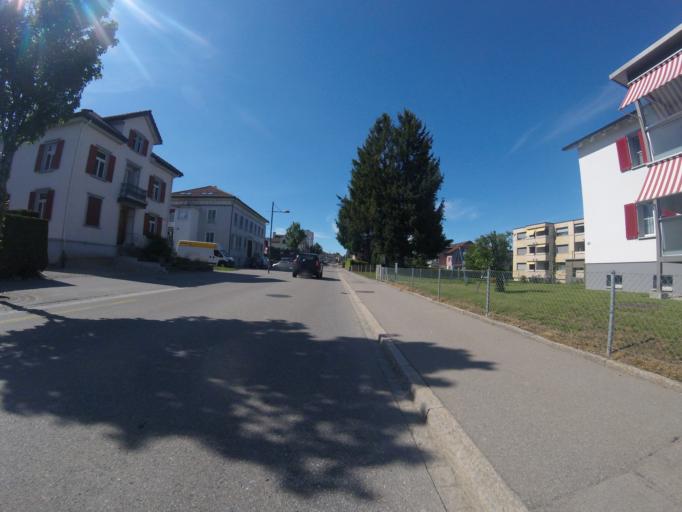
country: CH
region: Saint Gallen
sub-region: Wahlkreis Toggenburg
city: Lutisburg
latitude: 47.4101
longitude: 9.0703
